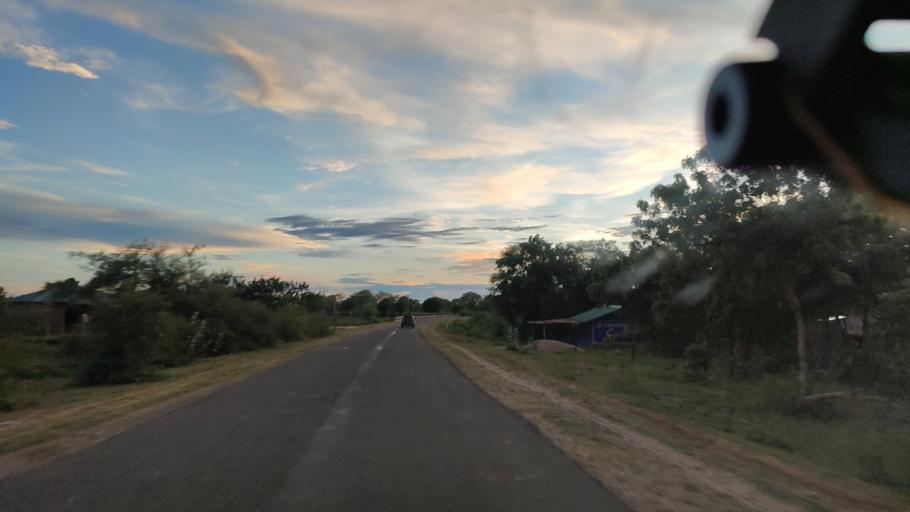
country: MM
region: Magway
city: Taungdwingyi
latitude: 20.1483
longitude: 95.5229
